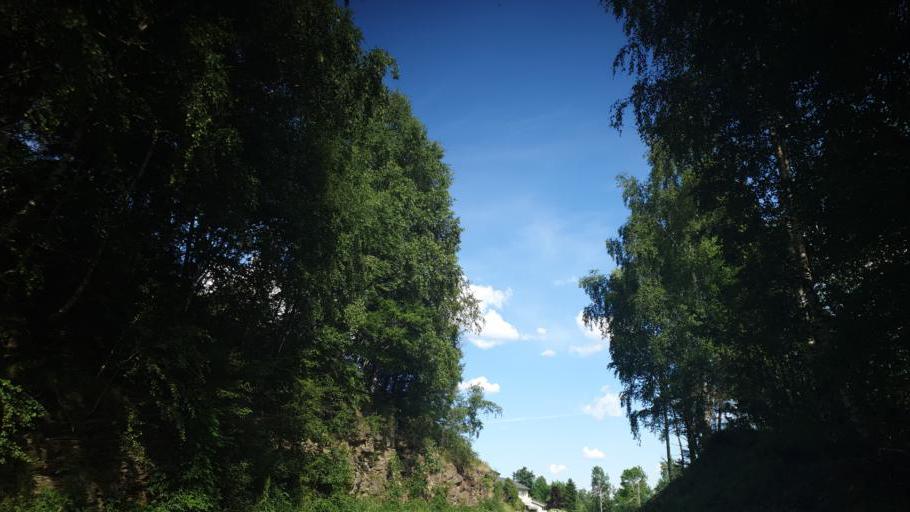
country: NO
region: Nord-Trondelag
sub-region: Leksvik
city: Leksvik
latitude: 63.6784
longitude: 10.6484
